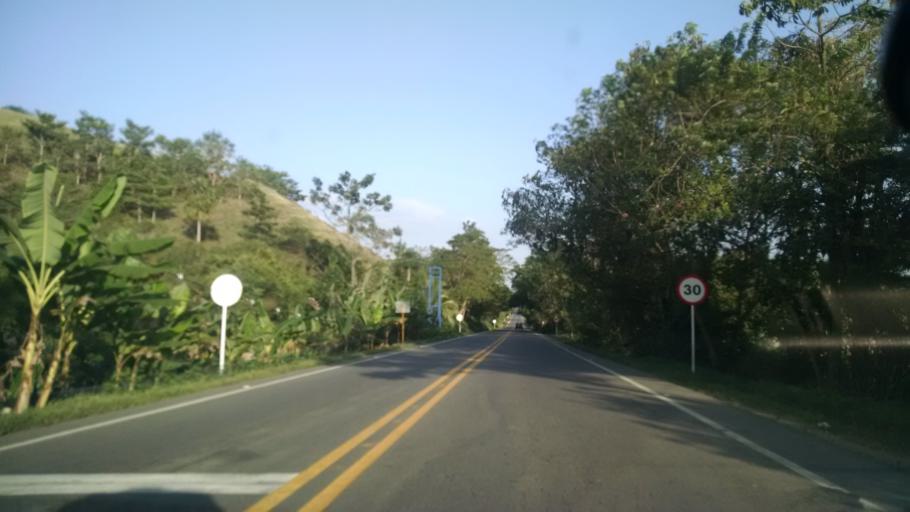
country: CO
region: Cordoba
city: Los Cordobas
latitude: 8.8485
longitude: -76.1943
